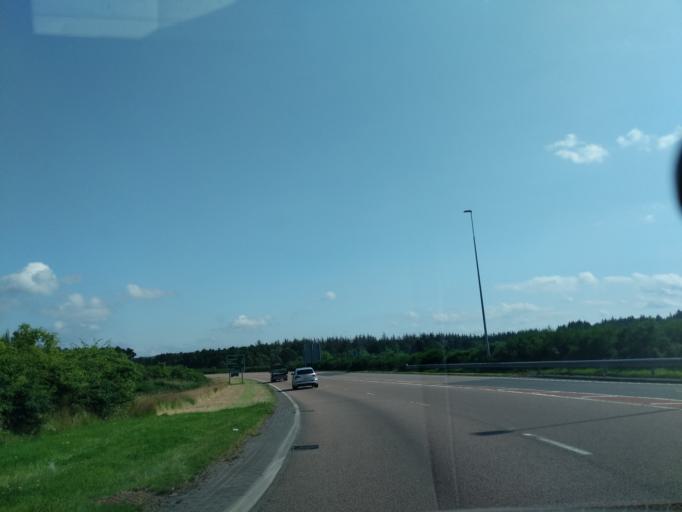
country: GB
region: Scotland
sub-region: Moray
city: Fochabers
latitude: 57.6262
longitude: -3.1415
